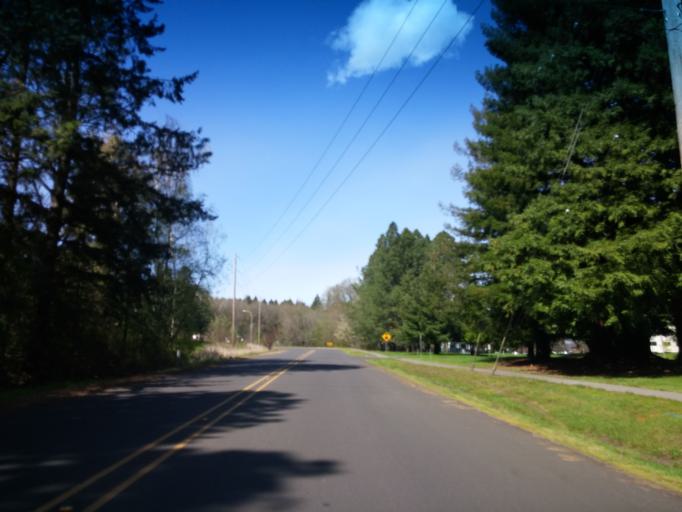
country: US
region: Oregon
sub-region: Washington County
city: Beaverton
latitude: 45.4987
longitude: -122.8277
